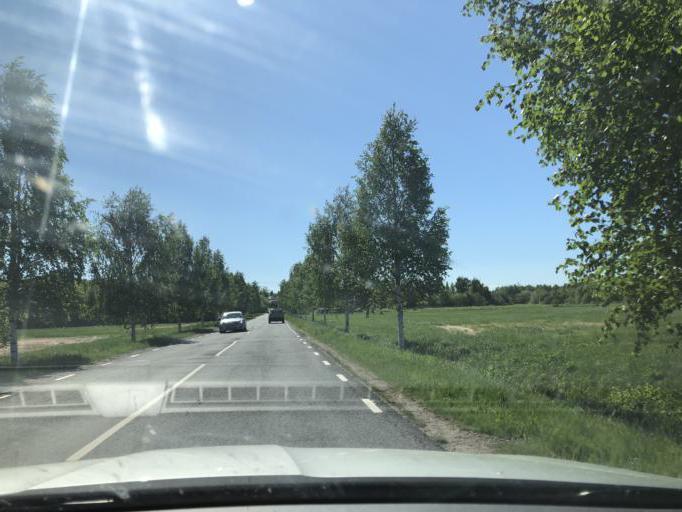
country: SE
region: Norrbotten
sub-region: Lulea Kommun
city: Gammelstad
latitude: 65.6503
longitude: 22.0193
